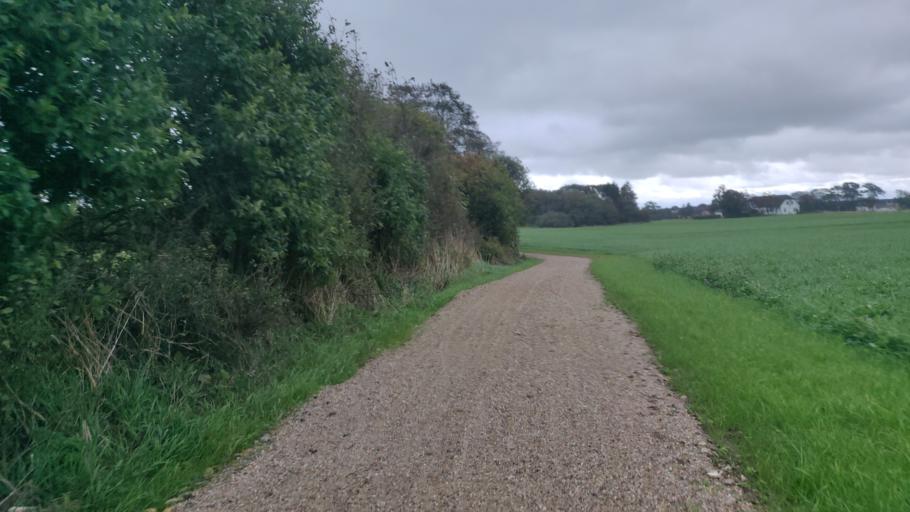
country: DK
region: South Denmark
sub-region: Kolding Kommune
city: Lunderskov
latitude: 55.5378
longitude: 9.3368
